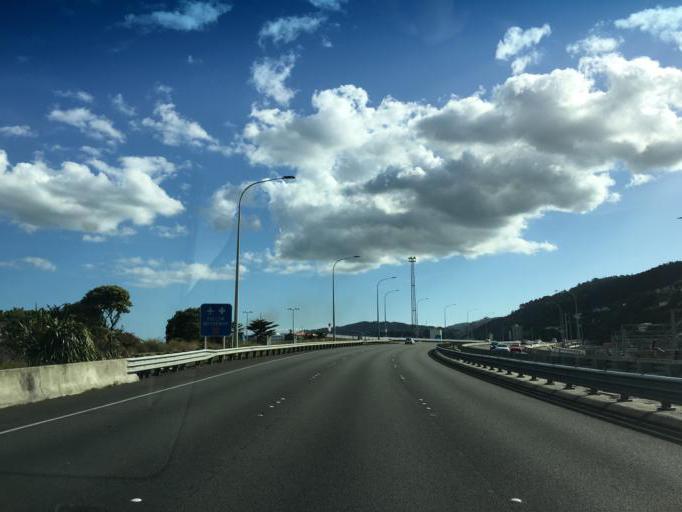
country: NZ
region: Wellington
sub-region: Wellington City
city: Wellington
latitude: -41.2605
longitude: 174.7918
